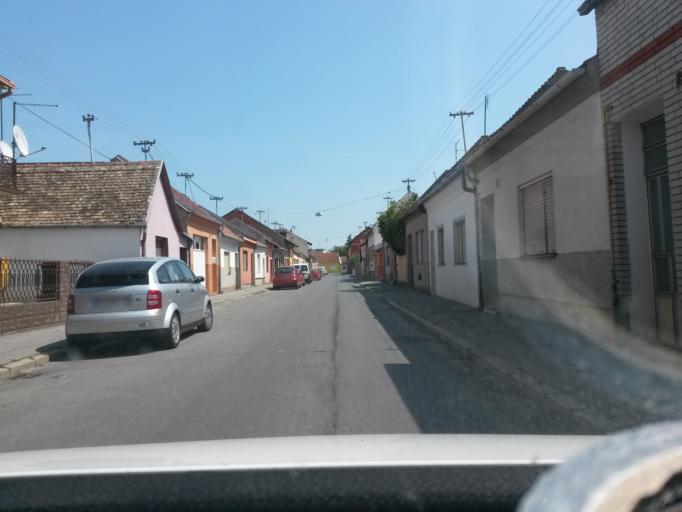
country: HR
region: Osjecko-Baranjska
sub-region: Grad Osijek
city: Osijek
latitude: 45.5605
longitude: 18.6561
